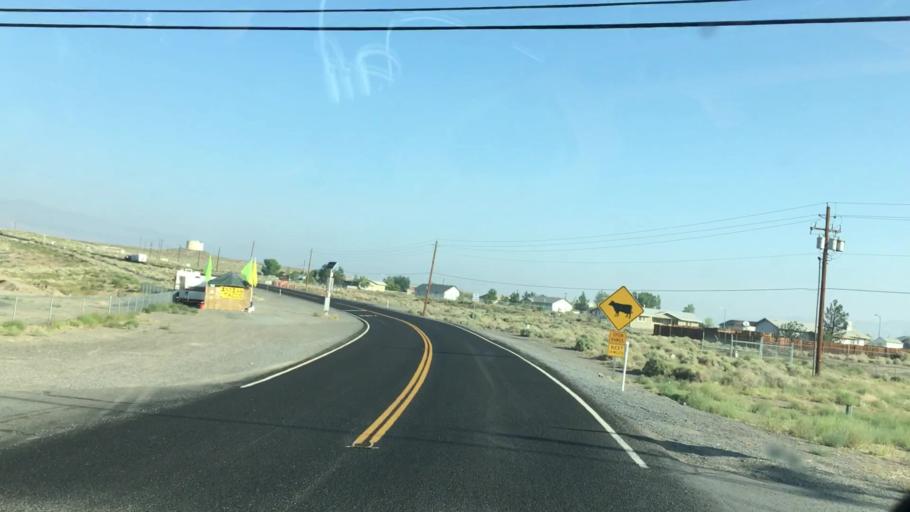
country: US
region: Nevada
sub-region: Lyon County
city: Fernley
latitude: 39.6367
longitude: -119.2908
